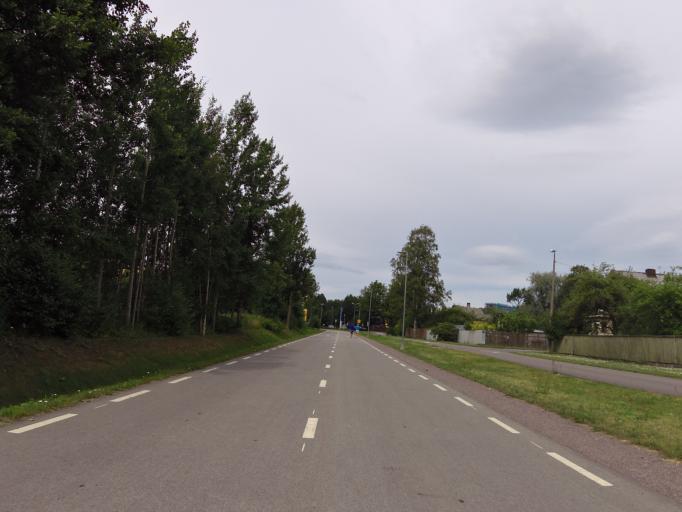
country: EE
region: Harju
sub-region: Tallinna linn
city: Tallinn
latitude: 59.4276
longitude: 24.6834
